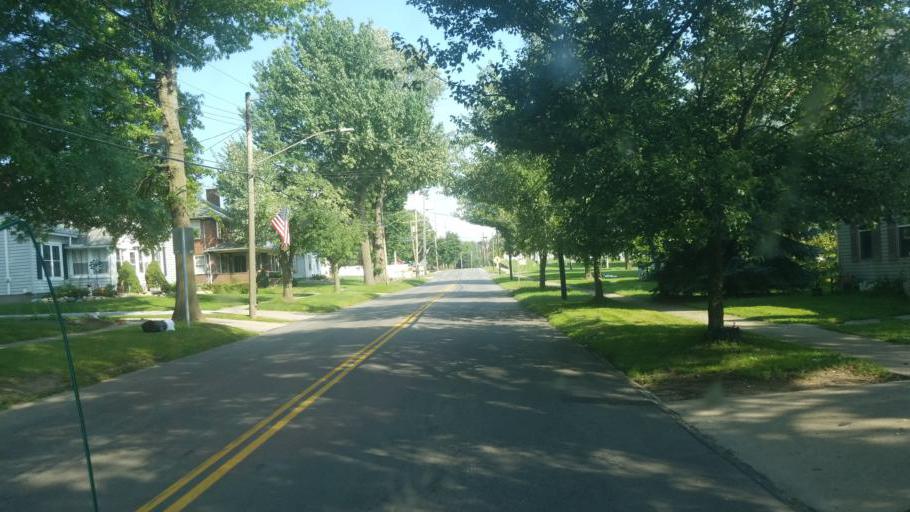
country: US
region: Ohio
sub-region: Medina County
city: Lodi
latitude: 41.0312
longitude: -82.0075
